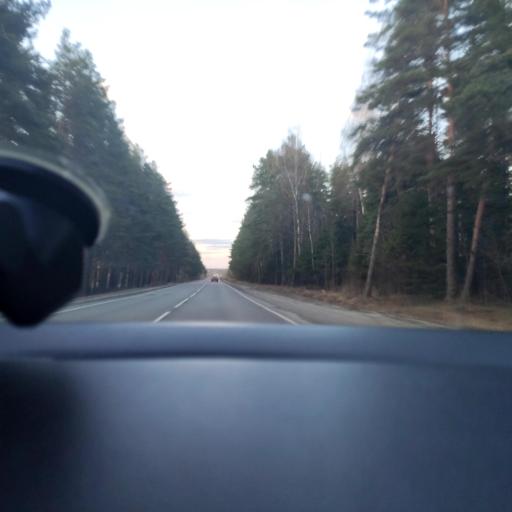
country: RU
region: Moskovskaya
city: Krasnyy Tkach
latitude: 55.4156
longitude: 39.1761
